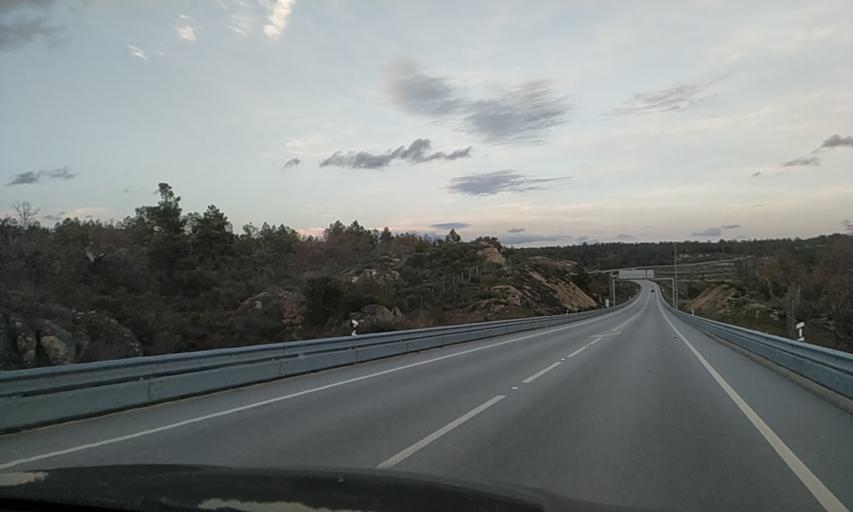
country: PT
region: Braganca
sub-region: Braganca Municipality
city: Vila Flor
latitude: 41.2705
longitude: -7.2059
